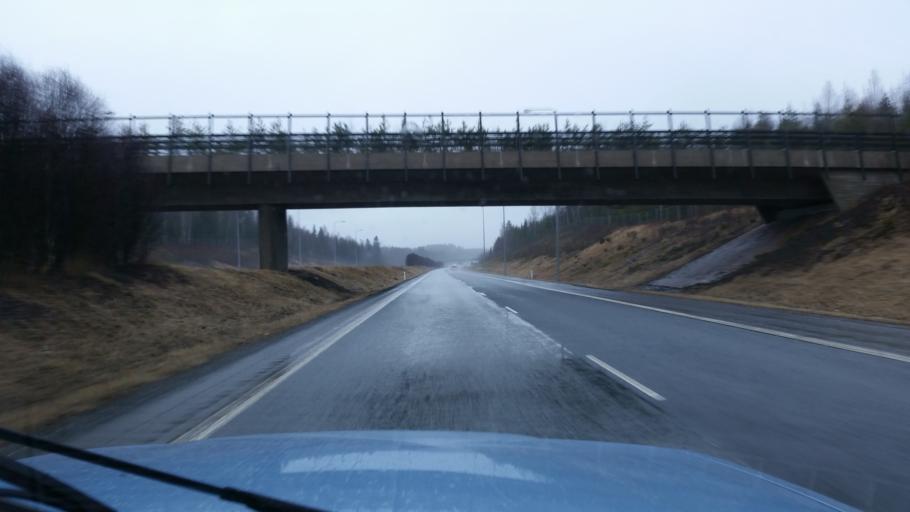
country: FI
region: Pirkanmaa
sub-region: Etelae-Pirkanmaa
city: Toijala
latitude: 61.2275
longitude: 23.8383
